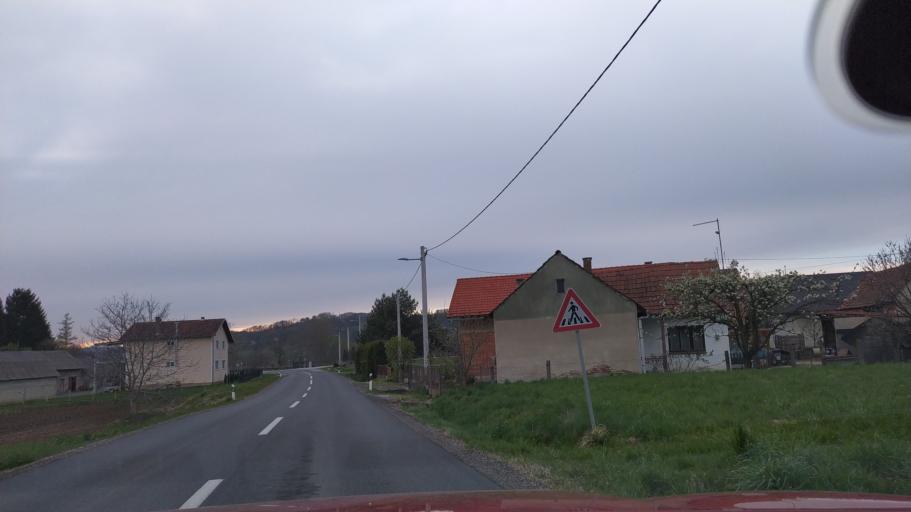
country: HR
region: Varazdinska
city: Jalzabet
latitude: 46.2111
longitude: 16.4734
